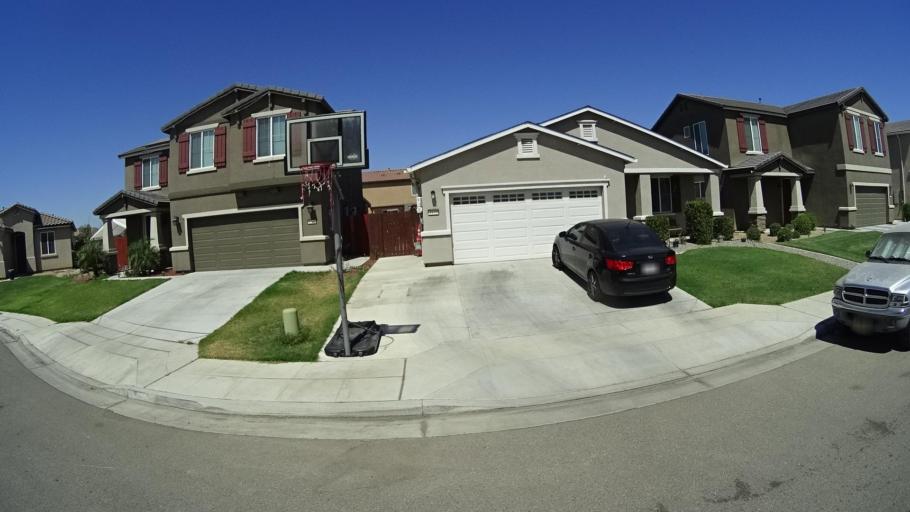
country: US
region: California
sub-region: Fresno County
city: Sunnyside
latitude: 36.7191
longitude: -119.6707
